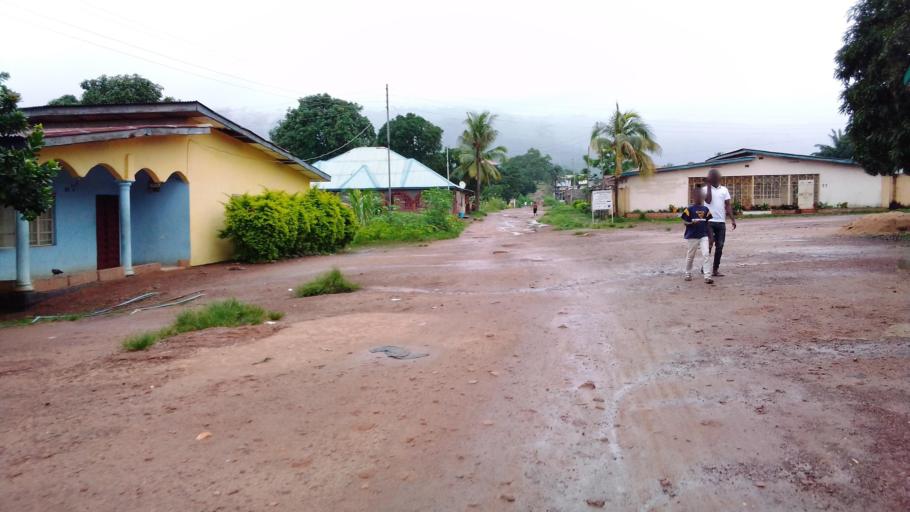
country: SL
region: Eastern Province
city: Kenema
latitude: 7.8963
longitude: -11.1793
